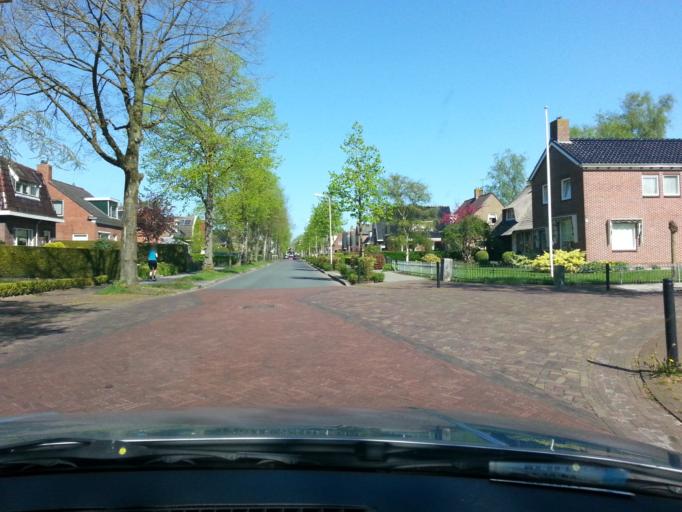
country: NL
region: Friesland
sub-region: Gemeente Achtkarspelen
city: Buitenpost
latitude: 53.2495
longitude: 6.1489
